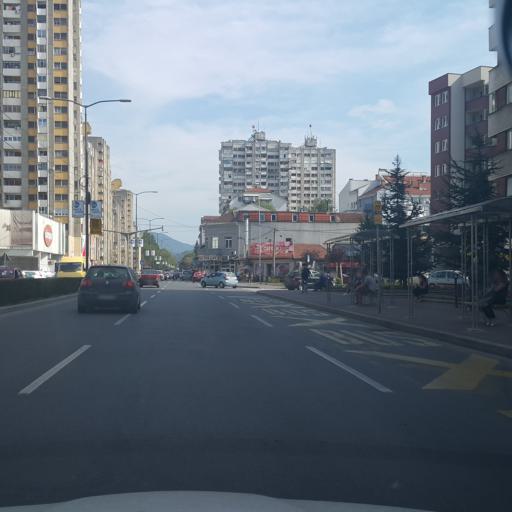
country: RS
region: Central Serbia
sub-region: Nisavski Okrug
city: Nis
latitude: 43.3193
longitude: 21.9077
